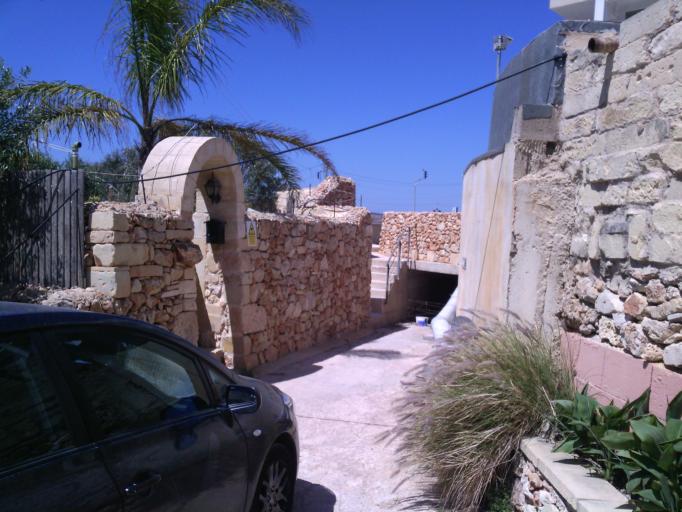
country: MT
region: Il-Mellieha
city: Mellieha
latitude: 35.9653
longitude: 14.3528
